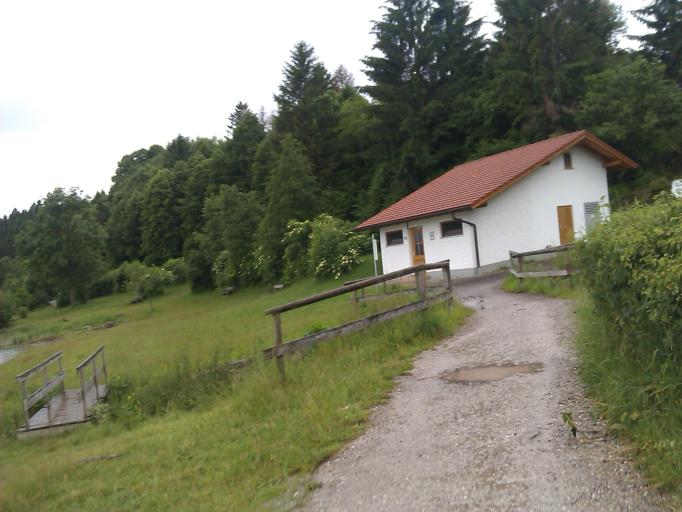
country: DE
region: Bavaria
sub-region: Swabia
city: Schwangau
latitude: 47.6085
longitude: 10.7181
